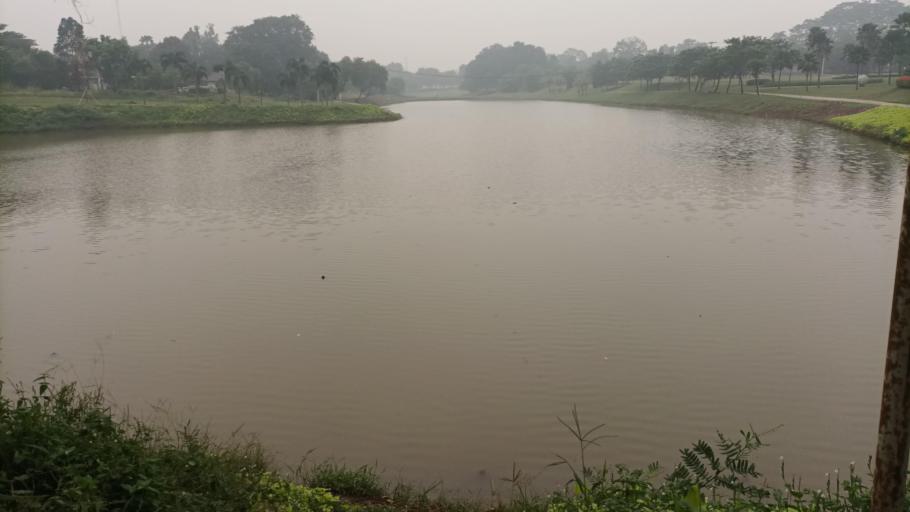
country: ID
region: West Java
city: Citeureup
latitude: -6.4213
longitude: 106.8914
